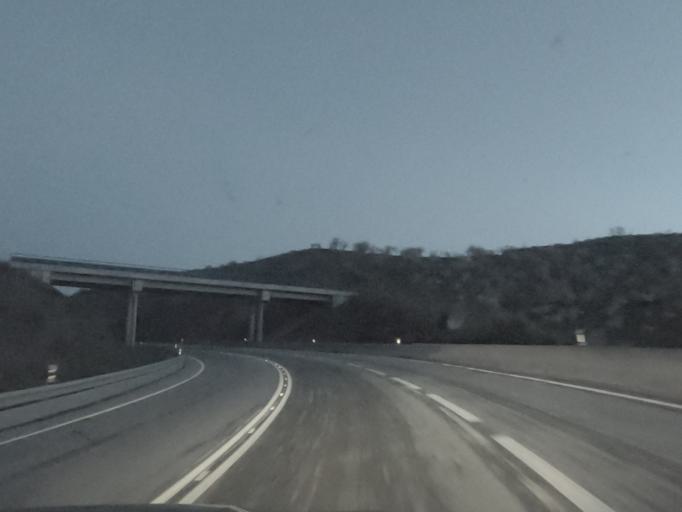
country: PT
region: Braganca
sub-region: Alfandega da Fe
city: Alfandega da Fe
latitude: 41.2766
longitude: -6.8740
